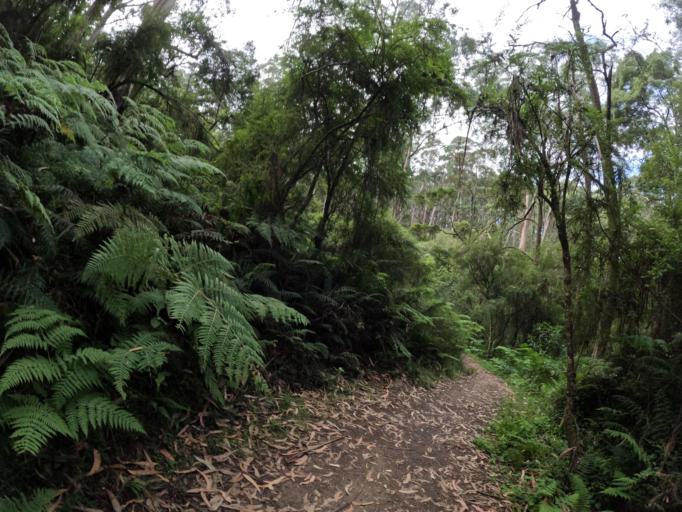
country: AU
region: Victoria
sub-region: Colac-Otway
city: Apollo Bay
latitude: -38.7893
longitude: 143.6202
